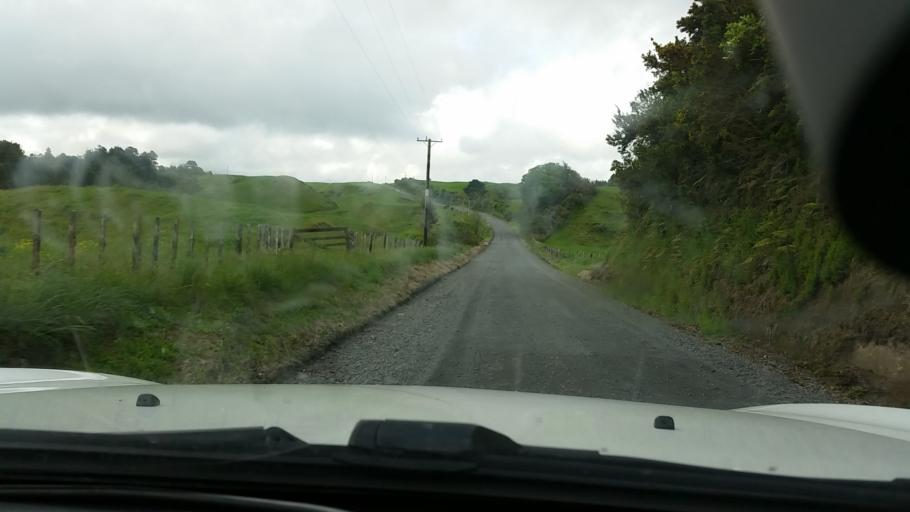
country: NZ
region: Bay of Plenty
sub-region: Rotorua District
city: Rotorua
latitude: -38.1430
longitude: 176.0815
